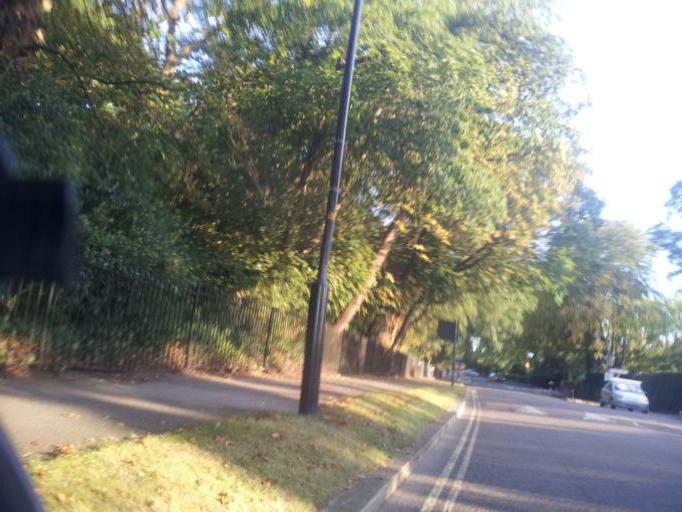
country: GB
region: England
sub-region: Greater London
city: Thornton Heath
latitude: 51.4302
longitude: -0.0782
